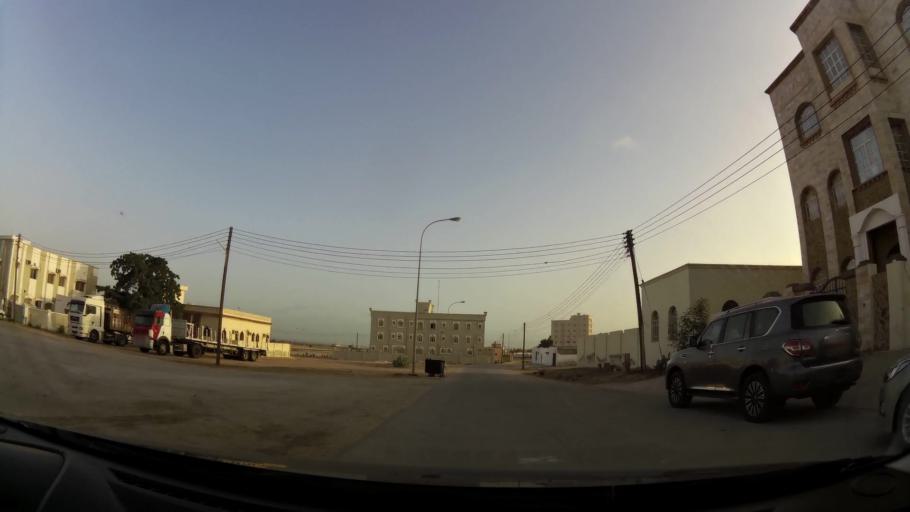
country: OM
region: Zufar
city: Salalah
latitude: 17.0006
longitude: 54.0340
